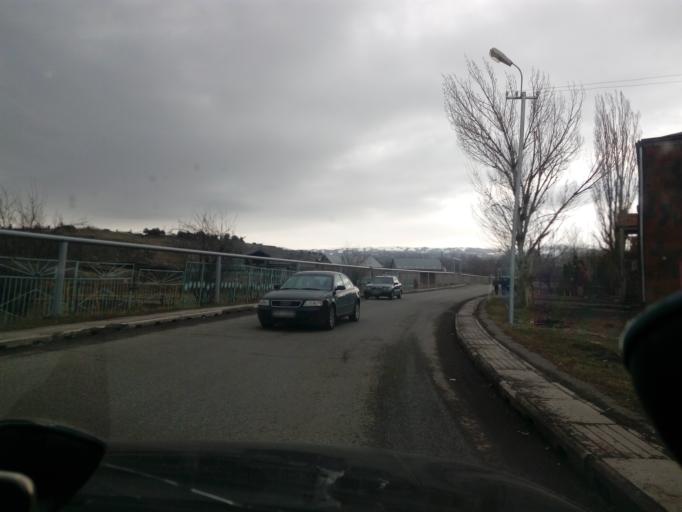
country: AM
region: Kotayk'i Marz
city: Kamaris
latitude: 40.2374
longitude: 44.6948
